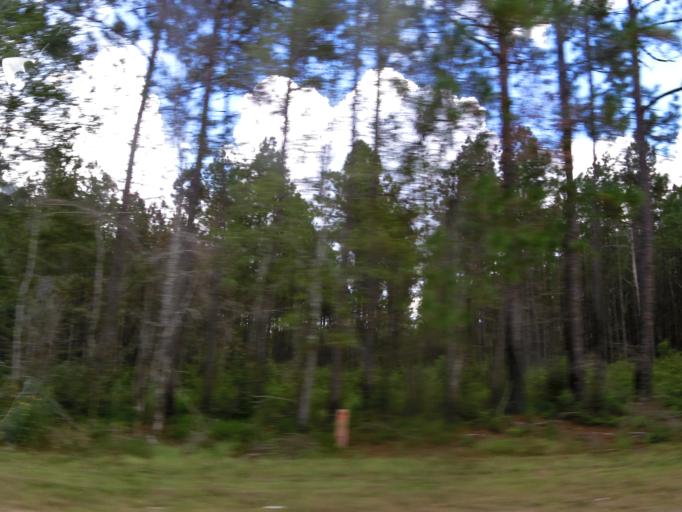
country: US
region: Georgia
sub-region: Charlton County
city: Folkston
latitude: 30.9647
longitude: -82.0241
